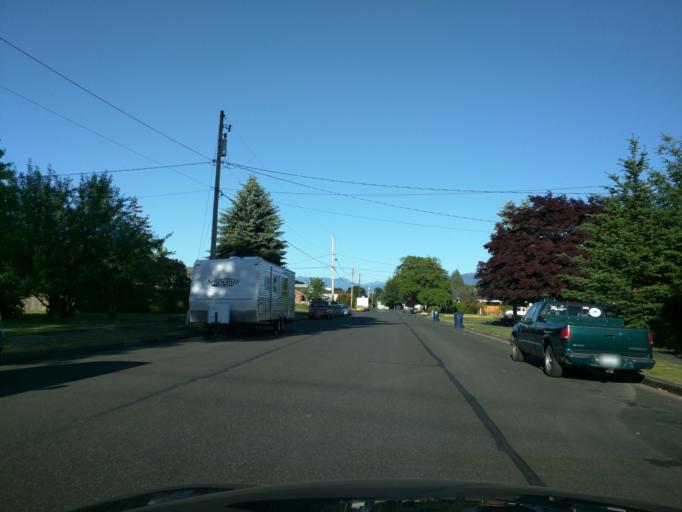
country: US
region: Washington
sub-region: Whatcom County
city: Lynden
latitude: 48.9379
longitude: -122.4677
